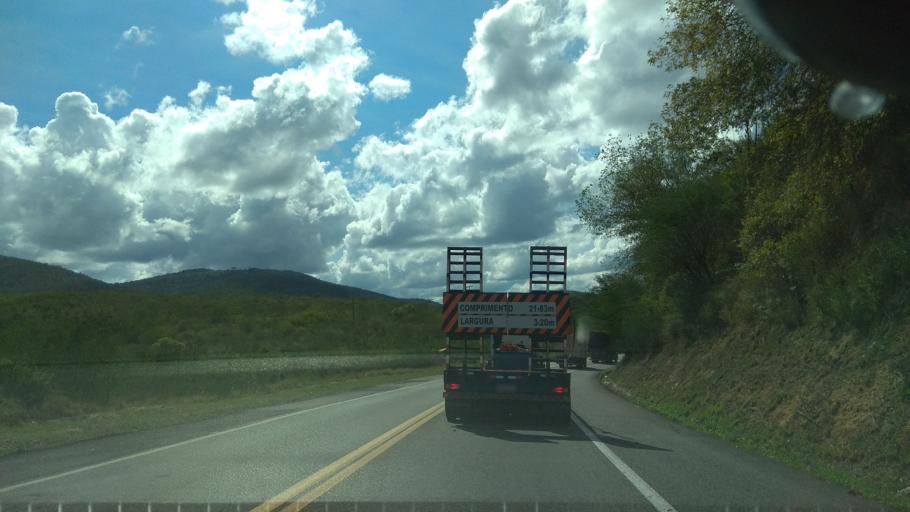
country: BR
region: Bahia
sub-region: Jequie
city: Jequie
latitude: -13.7686
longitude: -40.1025
